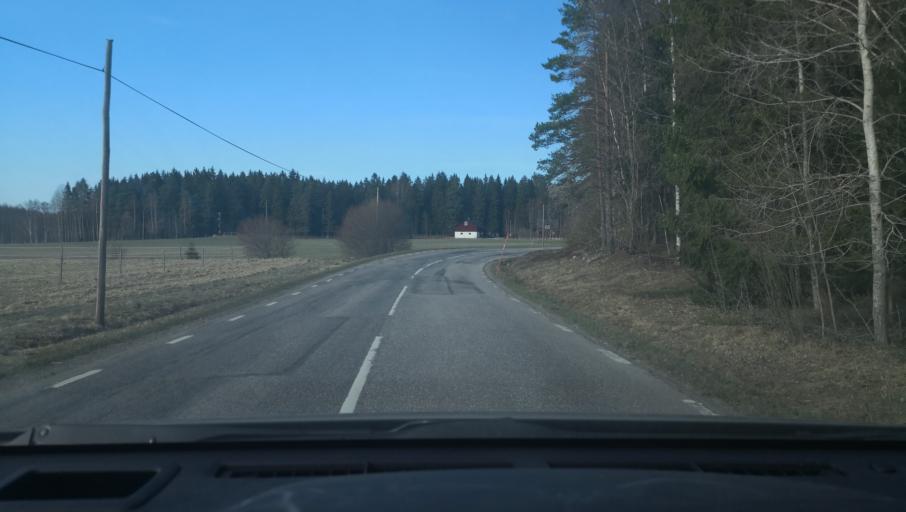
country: SE
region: Uppsala
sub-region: Heby Kommun
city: Heby
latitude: 59.9700
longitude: 16.8954
